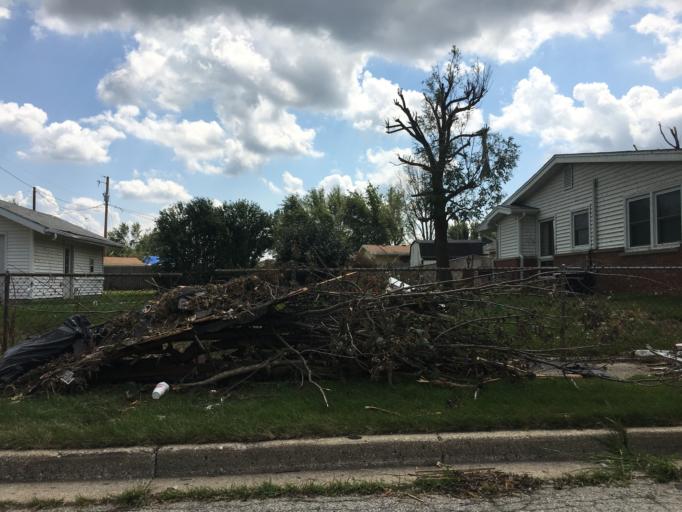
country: US
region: Indiana
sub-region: Howard County
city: Kokomo
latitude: 40.4705
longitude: -86.1047
